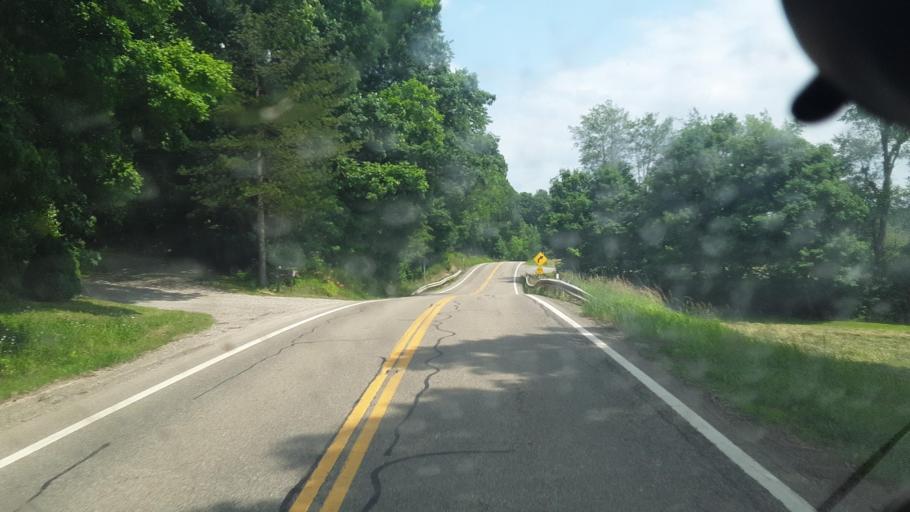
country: US
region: Ohio
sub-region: Coshocton County
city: West Lafayette
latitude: 40.3512
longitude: -81.7342
